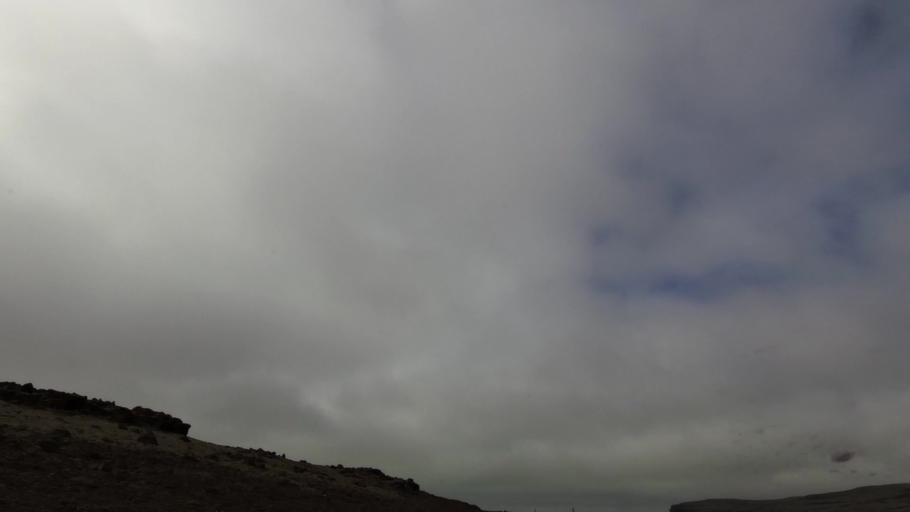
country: IS
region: West
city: Olafsvik
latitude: 65.5453
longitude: -24.3266
